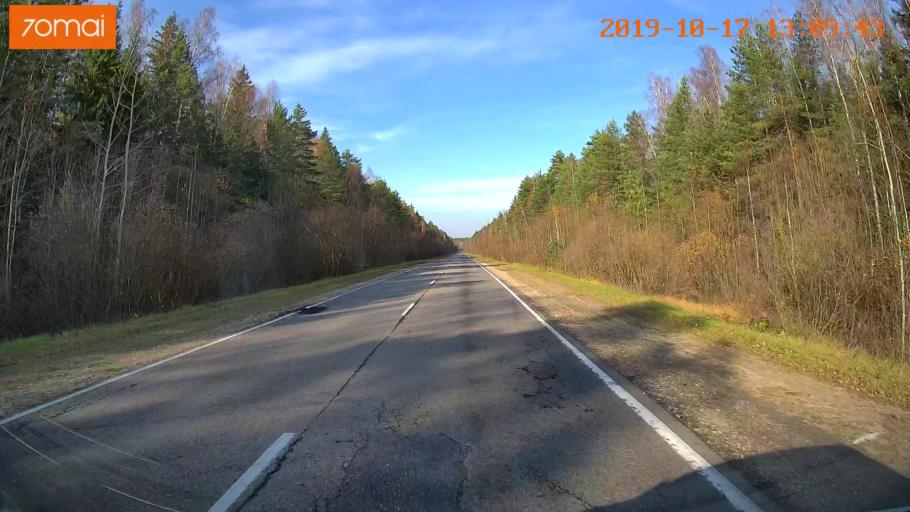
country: RU
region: Rjazan
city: Syntul
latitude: 55.0082
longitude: 41.2612
